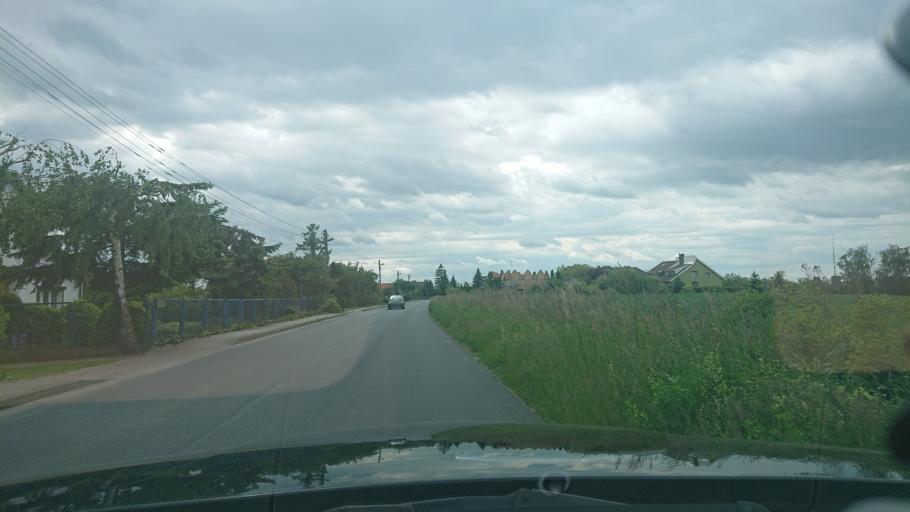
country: PL
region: Greater Poland Voivodeship
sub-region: Powiat gnieznienski
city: Gniezno
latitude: 52.5427
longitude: 17.5660
